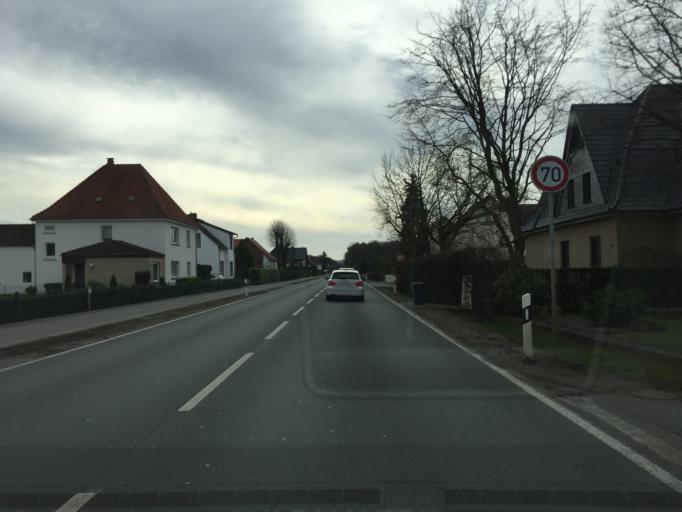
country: DE
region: North Rhine-Westphalia
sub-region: Regierungsbezirk Detmold
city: Lage
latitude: 52.0153
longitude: 8.7670
